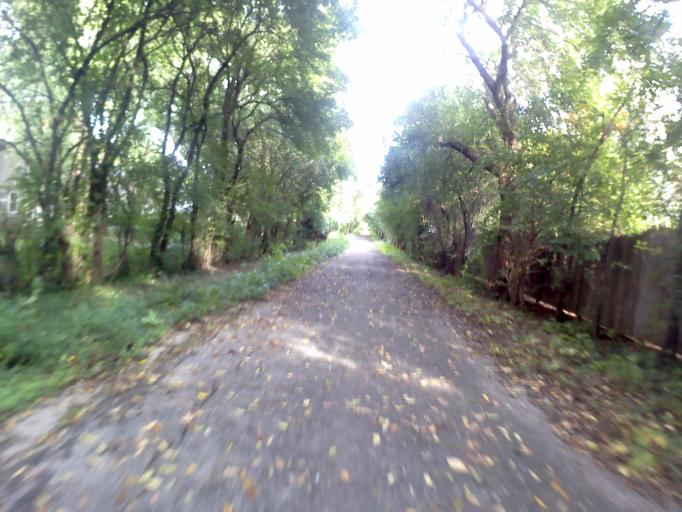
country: US
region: Illinois
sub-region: DuPage County
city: Wheaton
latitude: 41.8391
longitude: -88.1243
